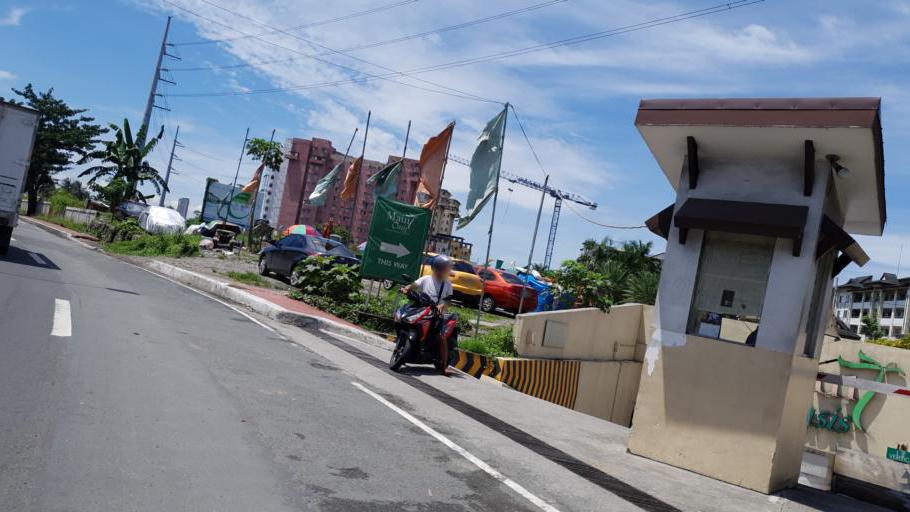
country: PH
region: Metro Manila
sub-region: San Juan
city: San Juan
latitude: 14.5979
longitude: 121.0137
